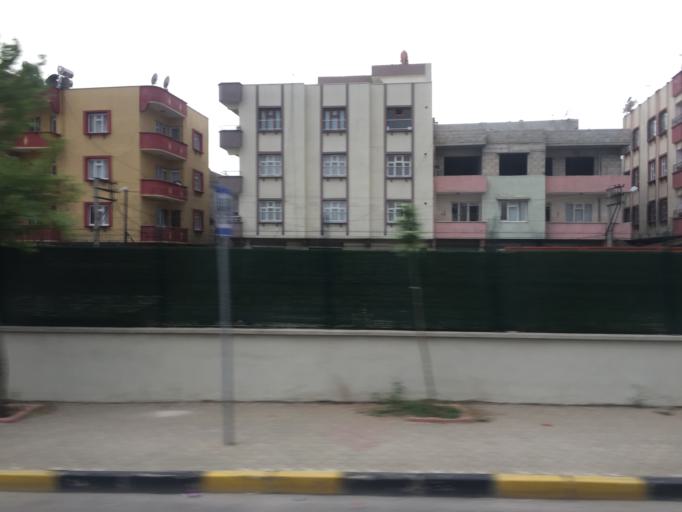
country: TR
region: Gaziantep
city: Gaziantep
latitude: 37.0637
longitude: 37.4152
